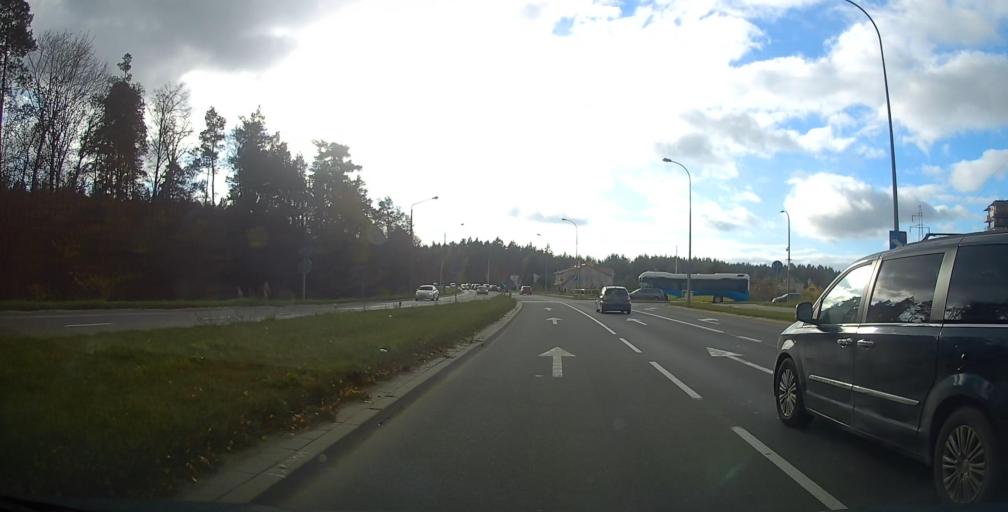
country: PL
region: Warmian-Masurian Voivodeship
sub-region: Powiat elcki
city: Elk
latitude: 53.7960
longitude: 22.3570
